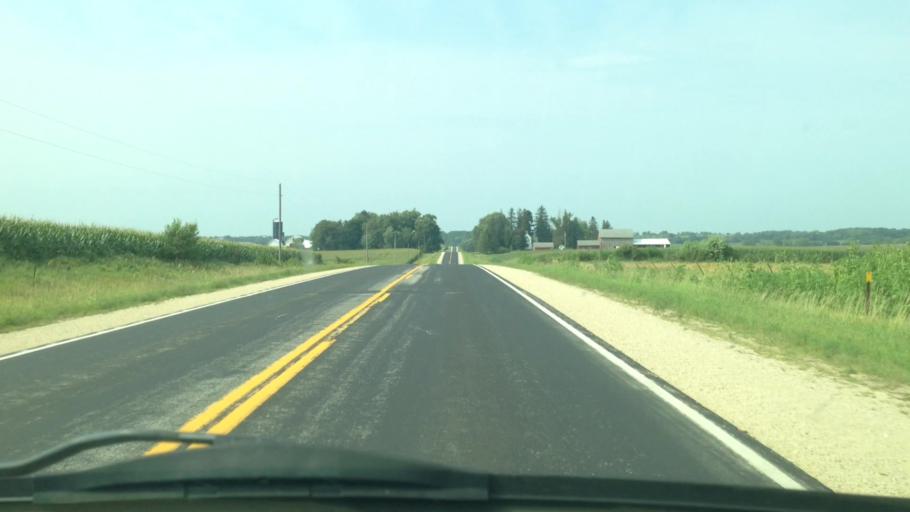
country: US
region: Minnesota
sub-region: Winona County
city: Lewiston
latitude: 43.9033
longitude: -91.9594
